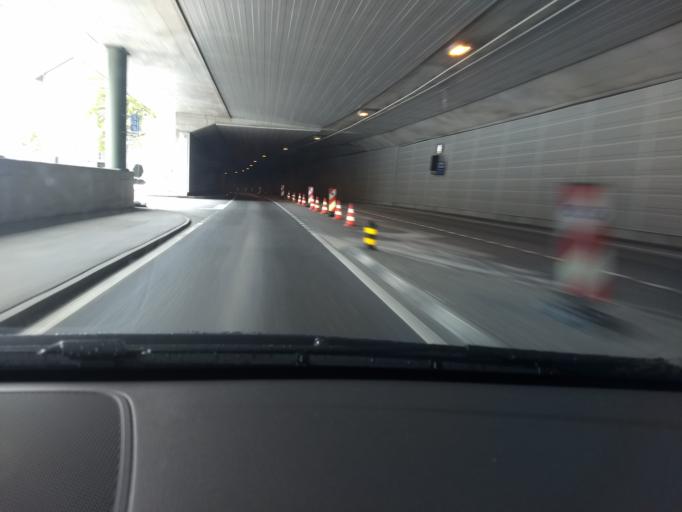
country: CH
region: Uri
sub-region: Uri
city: Andermatt
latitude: 46.6649
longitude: 8.5914
